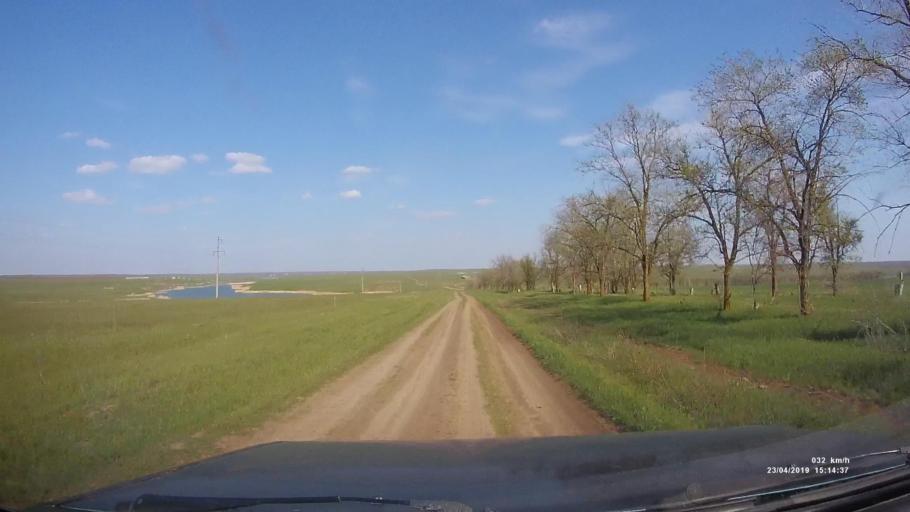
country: RU
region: Rostov
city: Remontnoye
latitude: 46.5397
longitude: 42.9645
